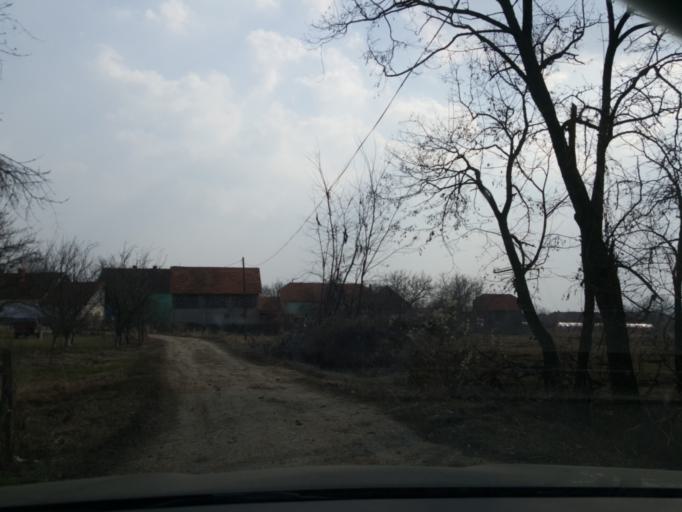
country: RS
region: Central Serbia
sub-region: Nisavski Okrug
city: Aleksinac
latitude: 43.4536
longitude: 21.7868
